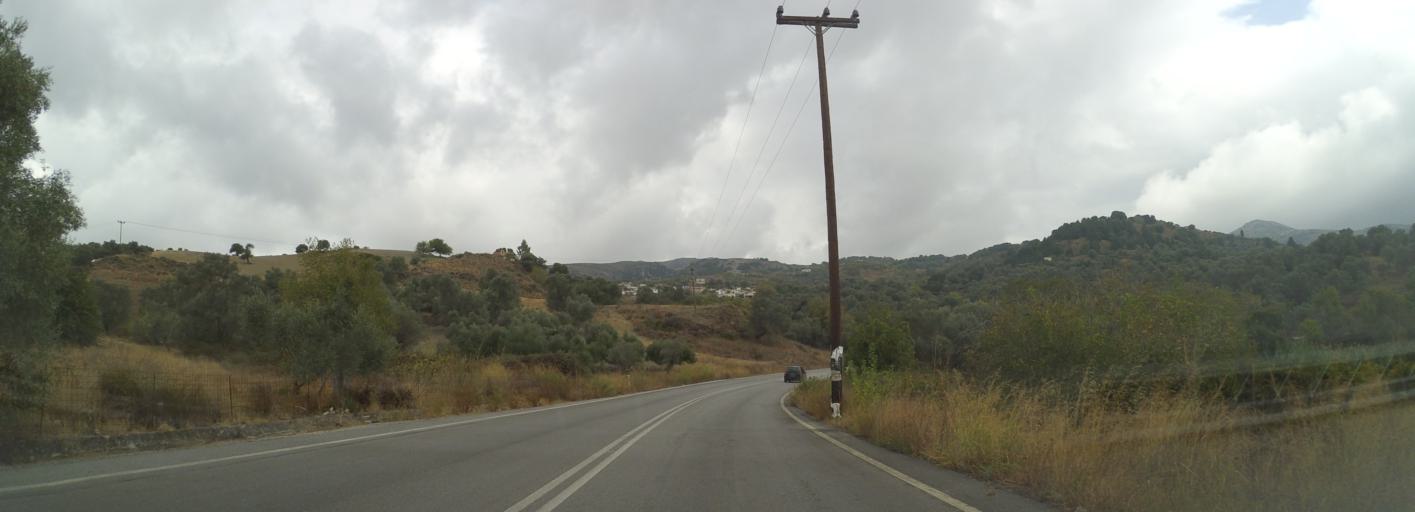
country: GR
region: Crete
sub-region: Nomos Rethymnis
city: Agia Foteini
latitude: 35.2205
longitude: 24.5090
